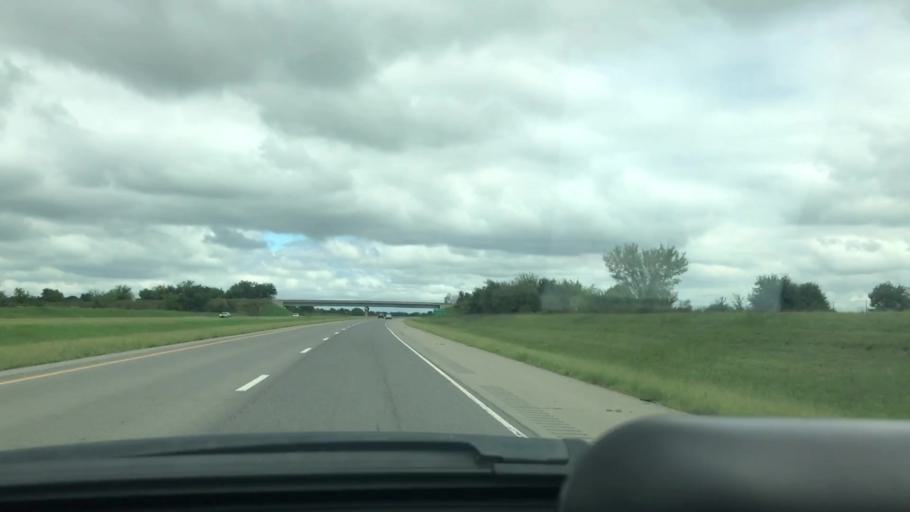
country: US
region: Oklahoma
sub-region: McIntosh County
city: Checotah
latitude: 35.5924
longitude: -95.4859
